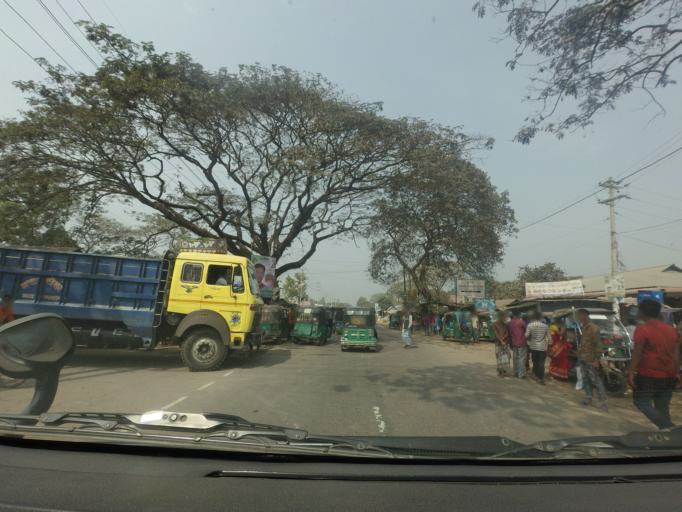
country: BD
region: Dhaka
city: Bajitpur
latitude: 24.1842
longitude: 90.8758
